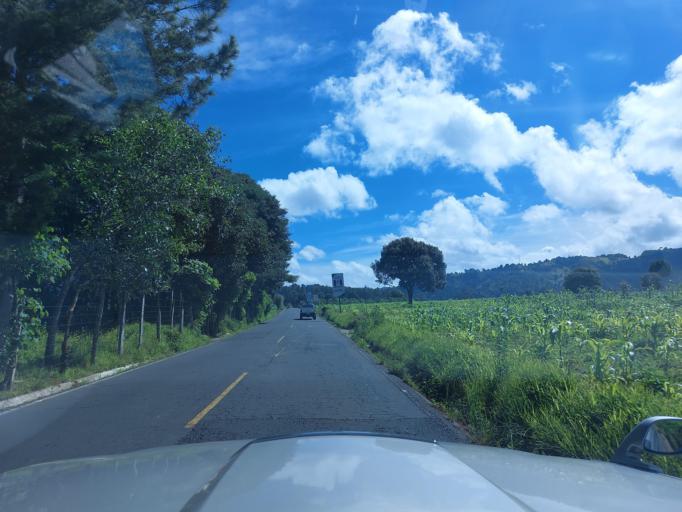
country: GT
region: Chimaltenango
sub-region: Municipio de Santa Cruz Balanya
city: Santa Cruz Balanya
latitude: 14.7012
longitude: -90.8986
